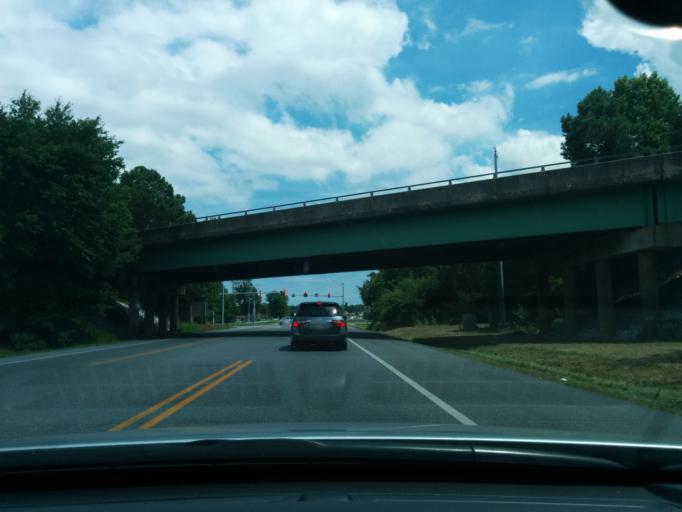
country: US
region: Maryland
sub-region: Worcester County
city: Ocean Pines
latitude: 38.3807
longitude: -75.1711
